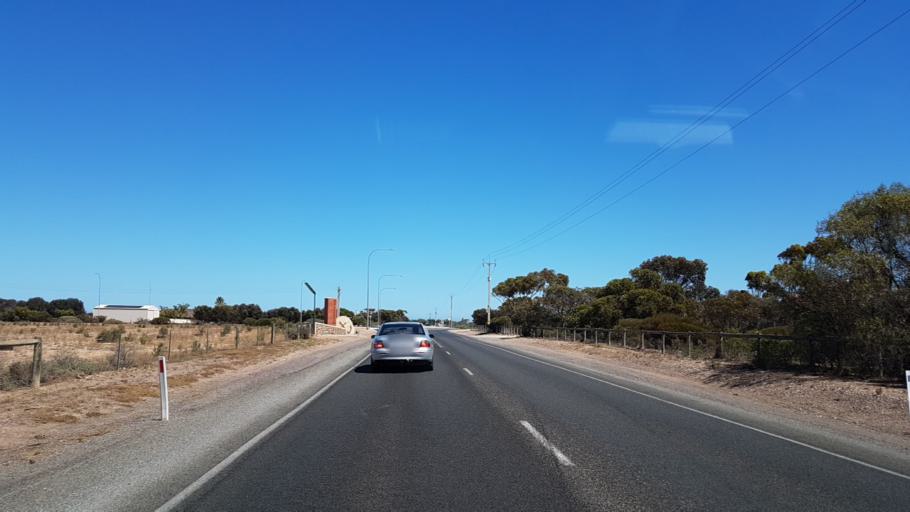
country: AU
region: South Australia
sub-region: Copper Coast
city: Wallaroo
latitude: -33.9414
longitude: 137.6541
